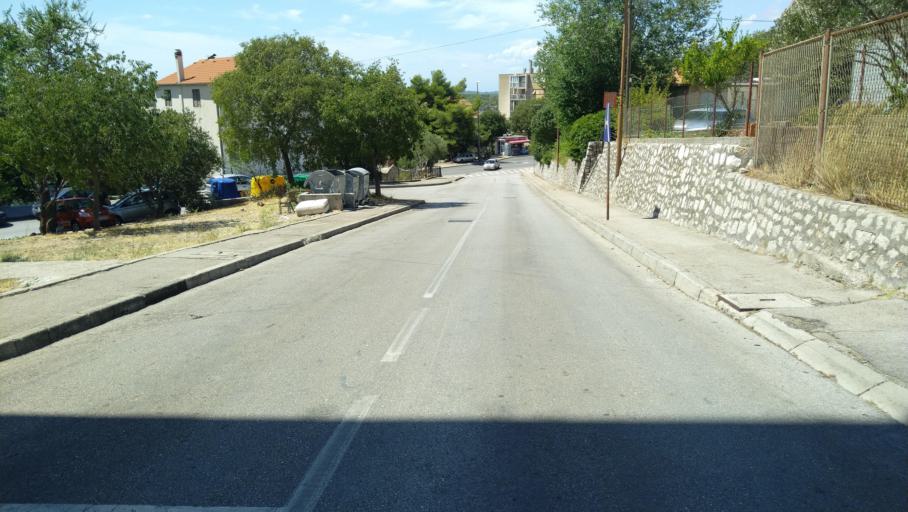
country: HR
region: Sibensko-Kniniska
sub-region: Grad Sibenik
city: Sibenik
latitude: 43.7253
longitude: 15.9070
